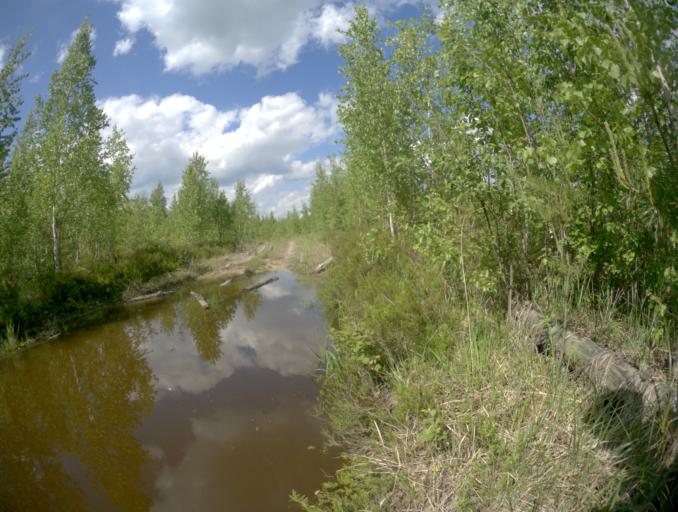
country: RU
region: Vladimir
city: Velikodvorskiy
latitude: 55.2896
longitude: 40.8912
